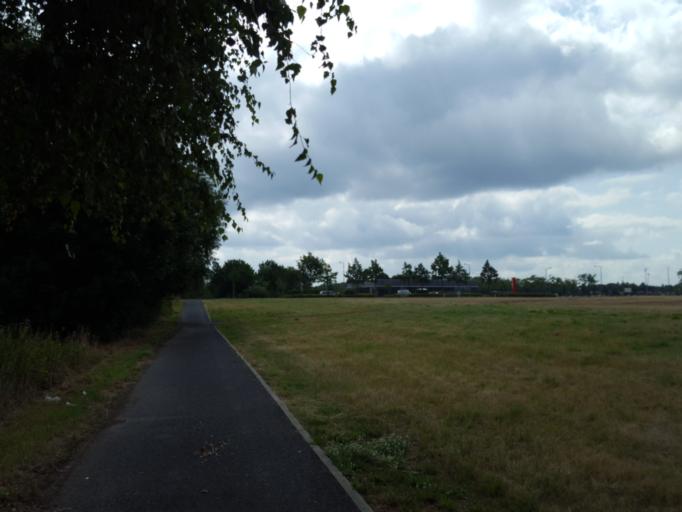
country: DE
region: Saxony
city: Albertstadt
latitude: 51.1269
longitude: 13.7373
